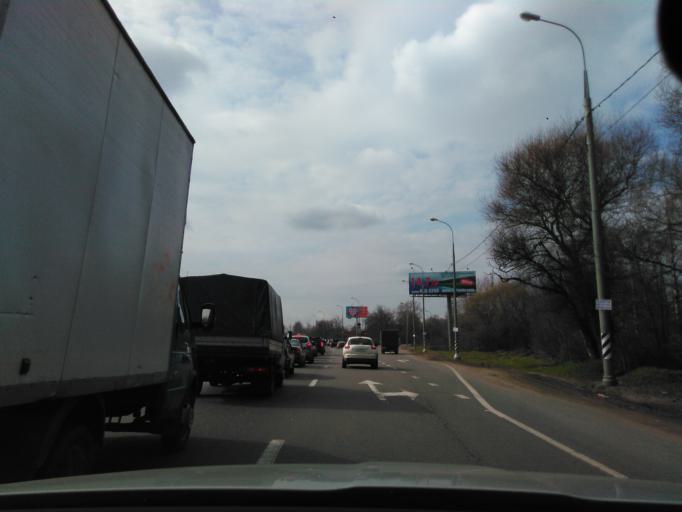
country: RU
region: Moskovskaya
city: Sheremet'yevskiy
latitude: 55.9802
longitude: 37.5255
